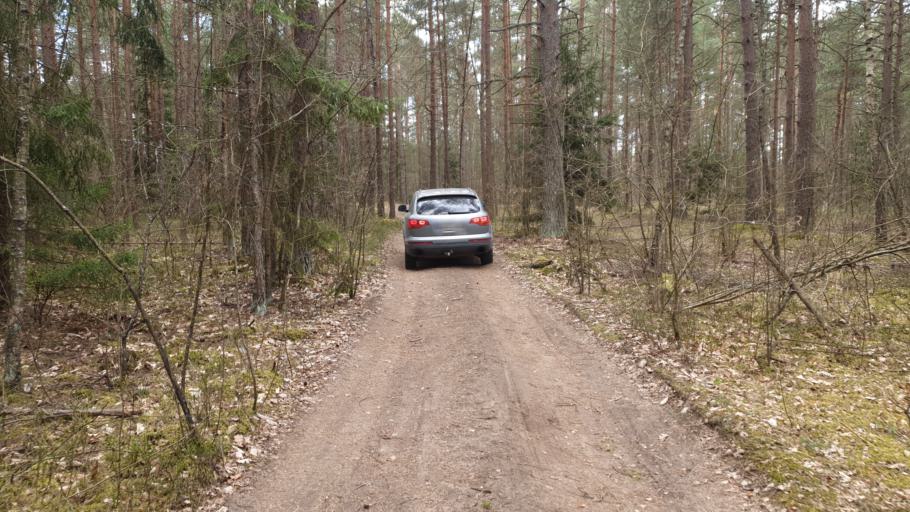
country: LT
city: Grigiskes
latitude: 54.7263
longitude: 25.0313
